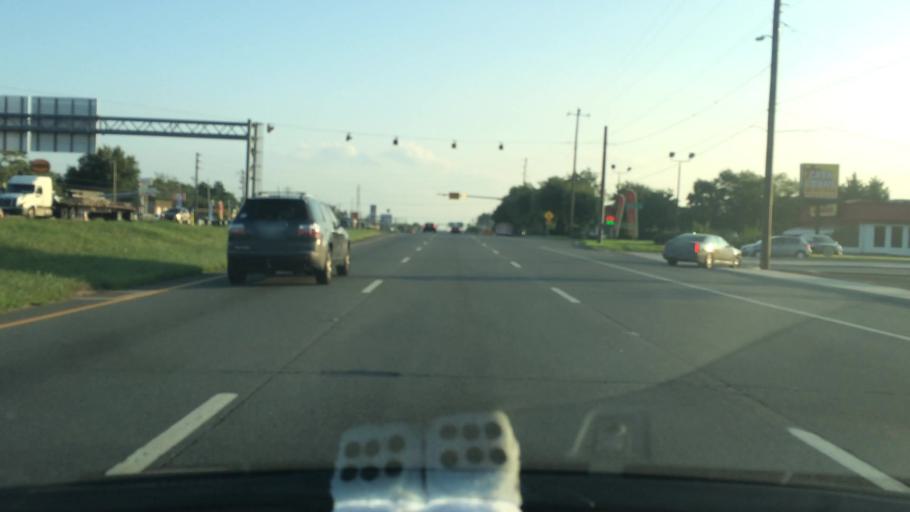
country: US
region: Delaware
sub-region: New Castle County
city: Wilmington Manor
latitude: 39.6937
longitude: -75.5786
